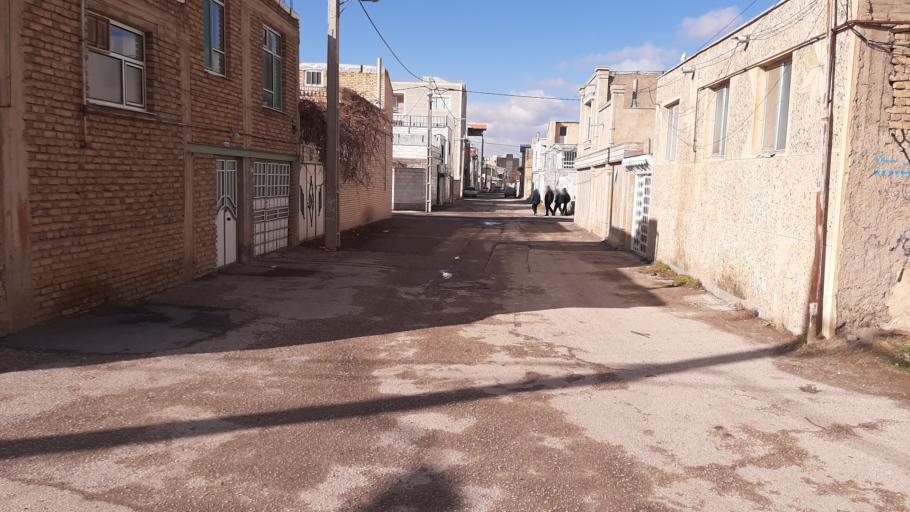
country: IR
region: Ardabil
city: Khalkhal
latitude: 37.6093
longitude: 48.5348
